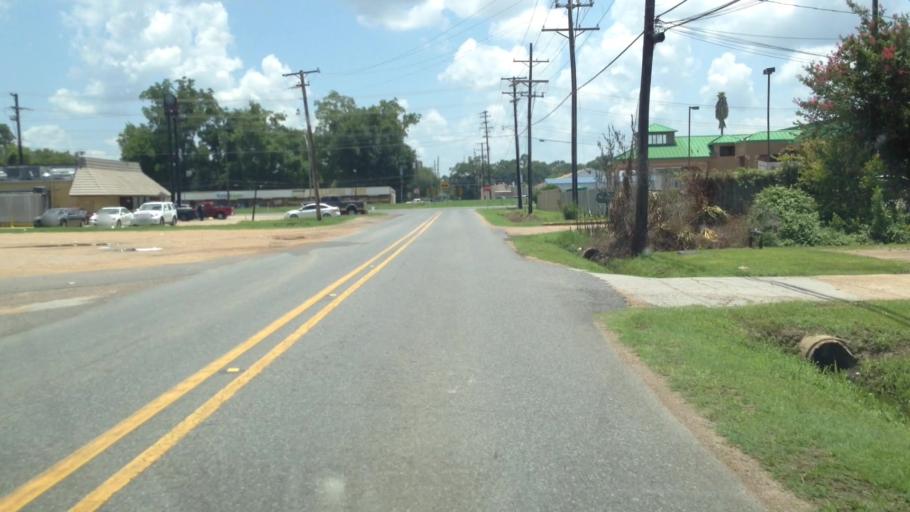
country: US
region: Louisiana
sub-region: Rapides Parish
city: Alexandria
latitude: 31.3115
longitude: -92.4790
